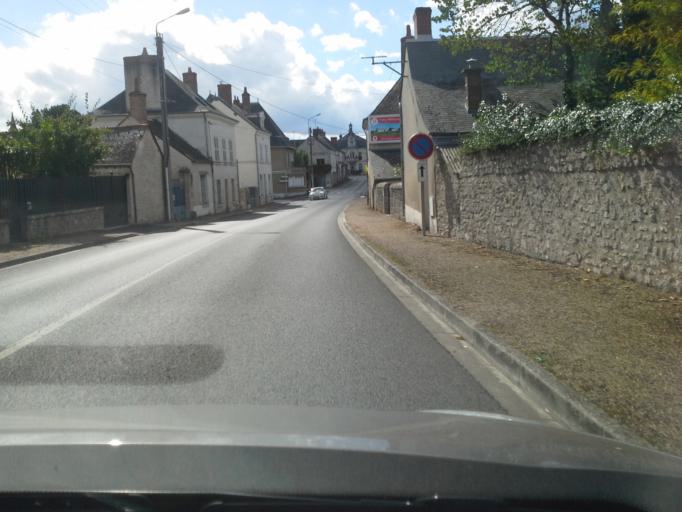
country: FR
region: Centre
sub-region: Departement du Loir-et-Cher
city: Pontlevoy
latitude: 47.3921
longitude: 1.2561
